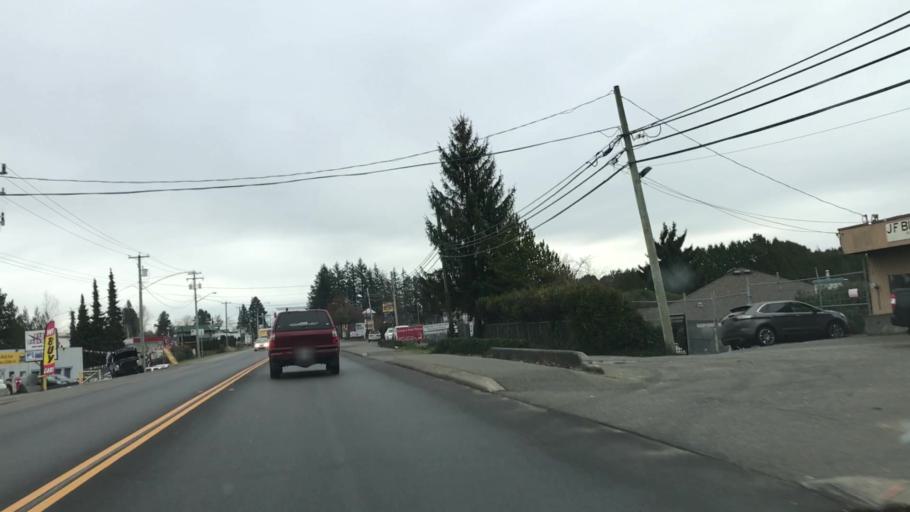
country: CA
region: British Columbia
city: Aldergrove
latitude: 49.0578
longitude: -122.4652
